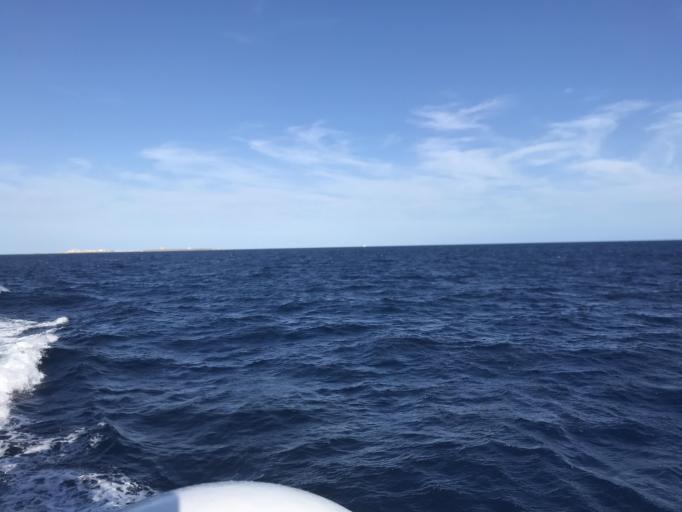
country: ES
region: Valencia
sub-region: Provincia de Alicante
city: Santa Pola
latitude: 38.1432
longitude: -0.5201
